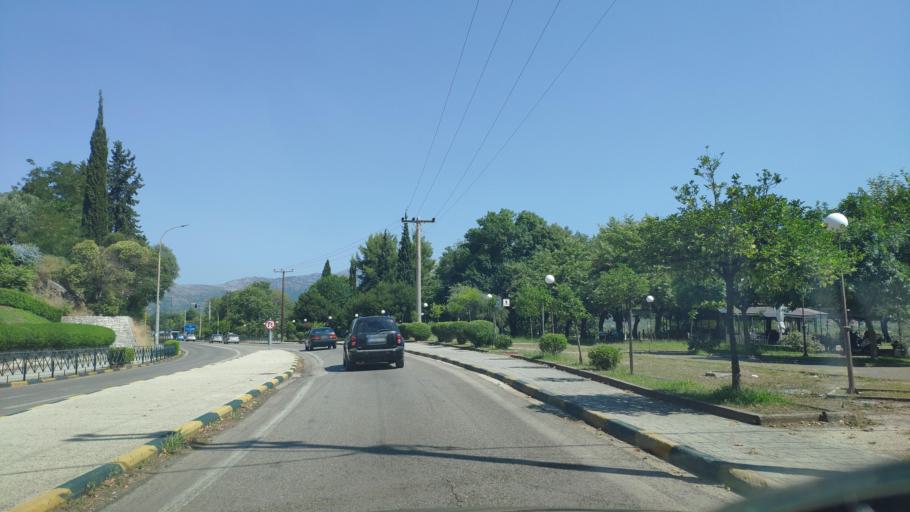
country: GR
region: Epirus
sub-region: Nomos Artas
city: Arta
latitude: 39.1598
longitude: 20.9952
